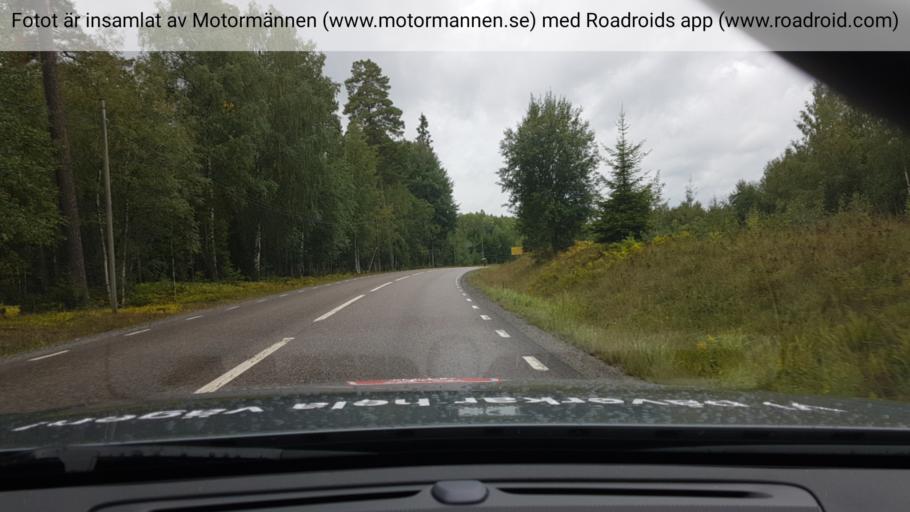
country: SE
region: Stockholm
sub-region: Botkyrka Kommun
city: Tullinge
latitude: 59.1764
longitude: 17.9292
